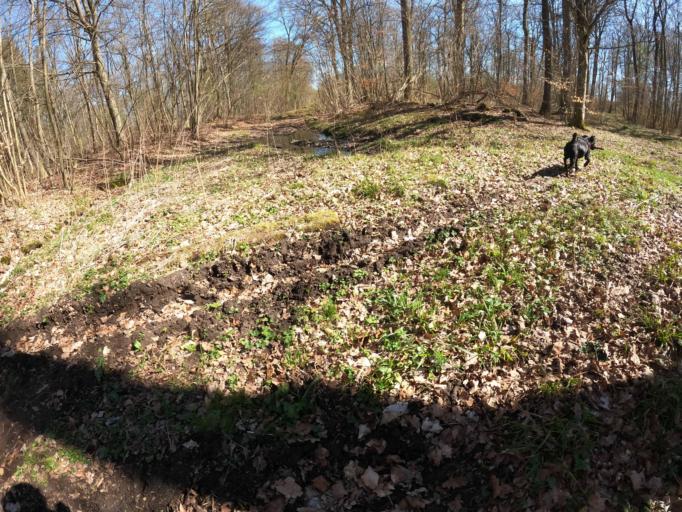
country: PL
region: West Pomeranian Voivodeship
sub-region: Powiat gryficki
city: Brojce
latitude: 53.9292
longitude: 15.2833
